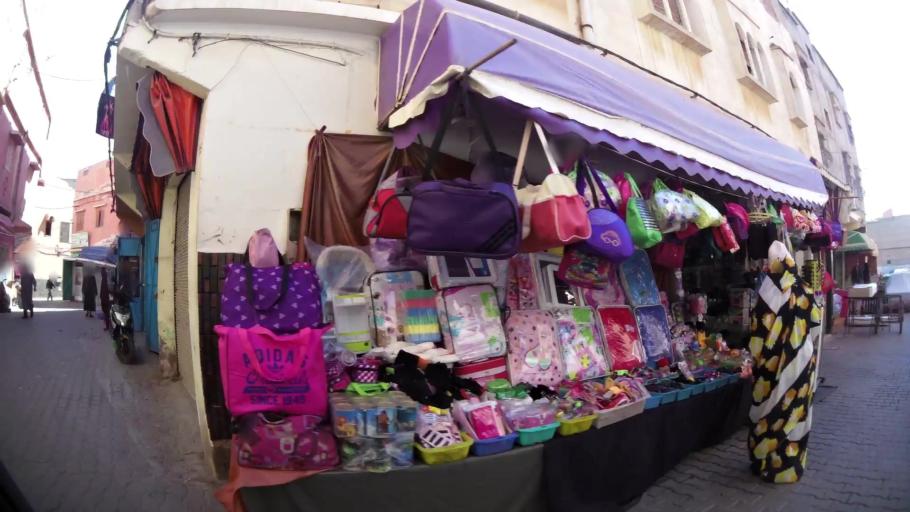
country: MA
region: Souss-Massa-Draa
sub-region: Inezgane-Ait Mellou
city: Inezgane
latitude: 30.3463
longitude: -9.5055
